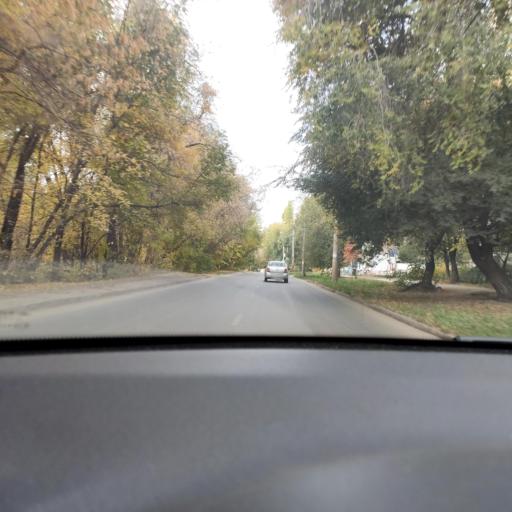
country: RU
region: Samara
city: Petra-Dubrava
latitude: 53.2468
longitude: 50.2586
